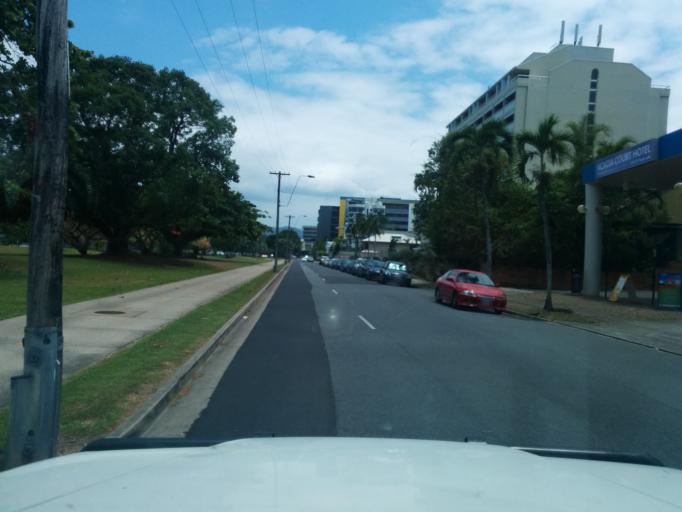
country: AU
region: Queensland
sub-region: Cairns
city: Cairns
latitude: -16.9088
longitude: 145.7654
